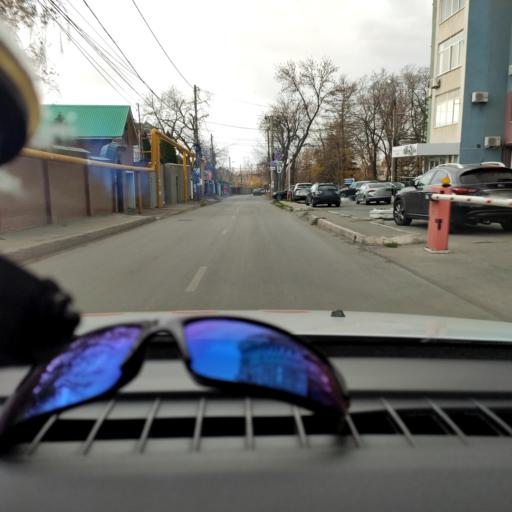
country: RU
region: Samara
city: Samara
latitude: 53.2336
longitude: 50.1799
